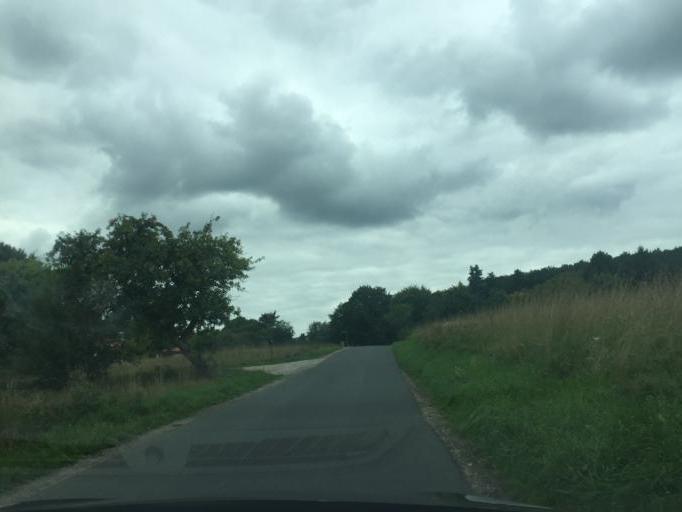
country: DK
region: South Denmark
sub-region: Assens Kommune
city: Tommerup
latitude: 55.3559
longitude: 10.2270
